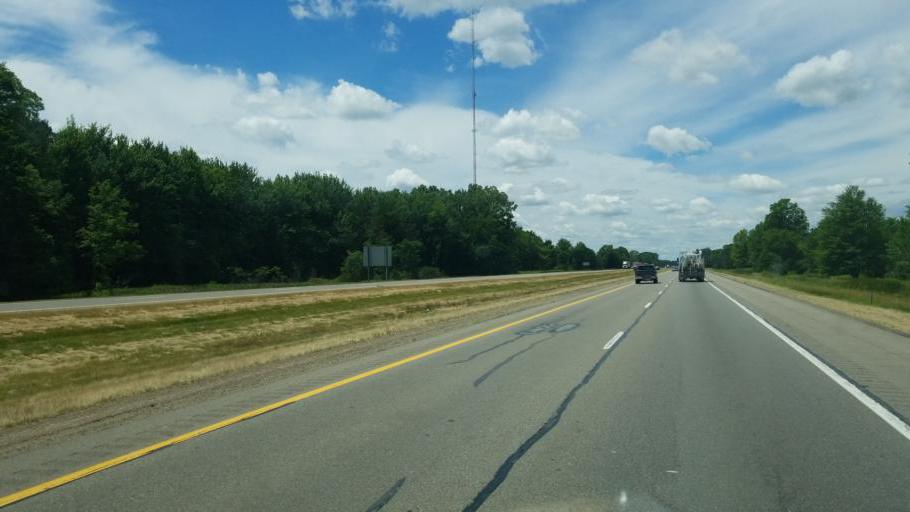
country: US
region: Michigan
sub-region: Eaton County
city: Dimondale
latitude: 42.6658
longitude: -84.6071
